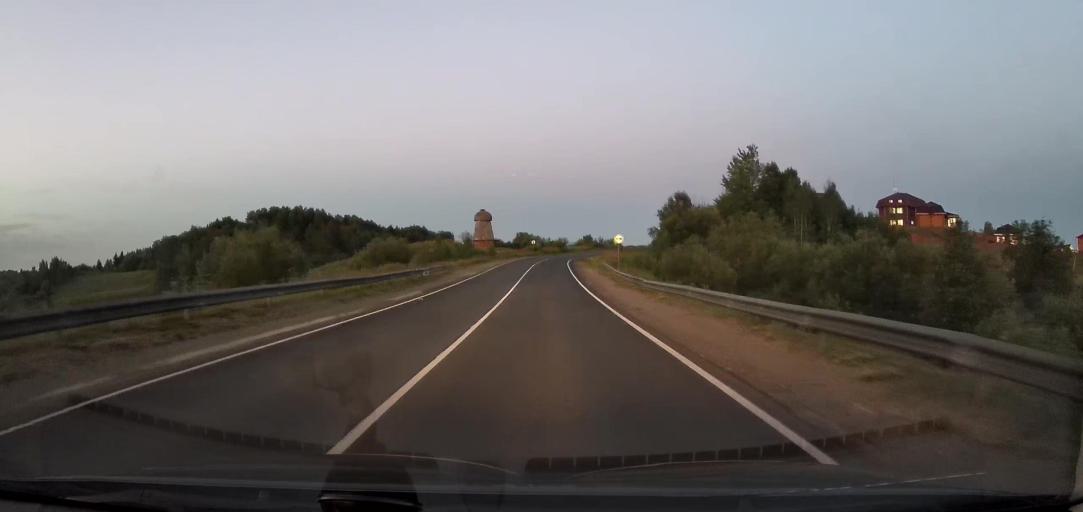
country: RU
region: Arkhangelskaya
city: Uyemskiy
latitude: 64.4503
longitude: 40.9429
